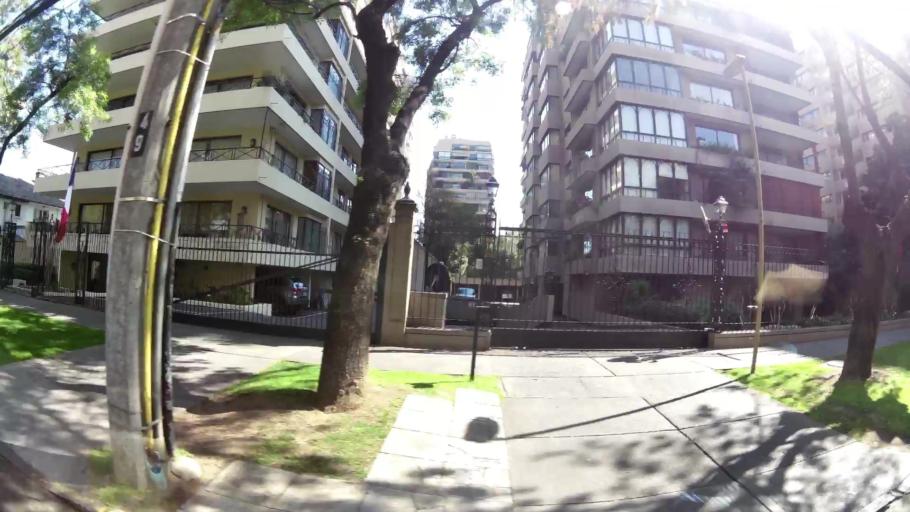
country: CL
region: Santiago Metropolitan
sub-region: Provincia de Santiago
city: Villa Presidente Frei, Nunoa, Santiago, Chile
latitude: -33.4175
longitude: -70.5874
